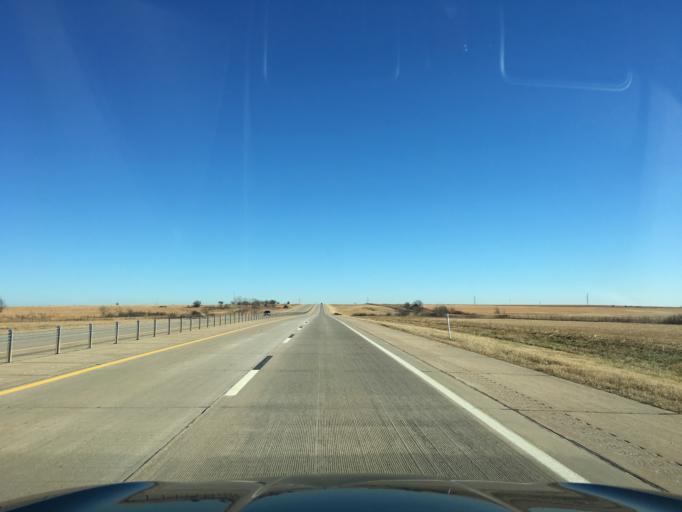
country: US
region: Oklahoma
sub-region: Noble County
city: Perry
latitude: 36.3921
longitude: -97.1297
